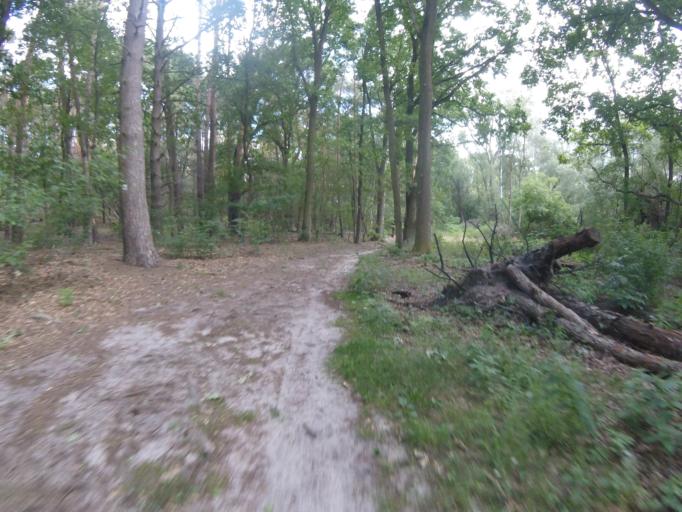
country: DE
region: Brandenburg
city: Bestensee
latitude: 52.2459
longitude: 13.6137
